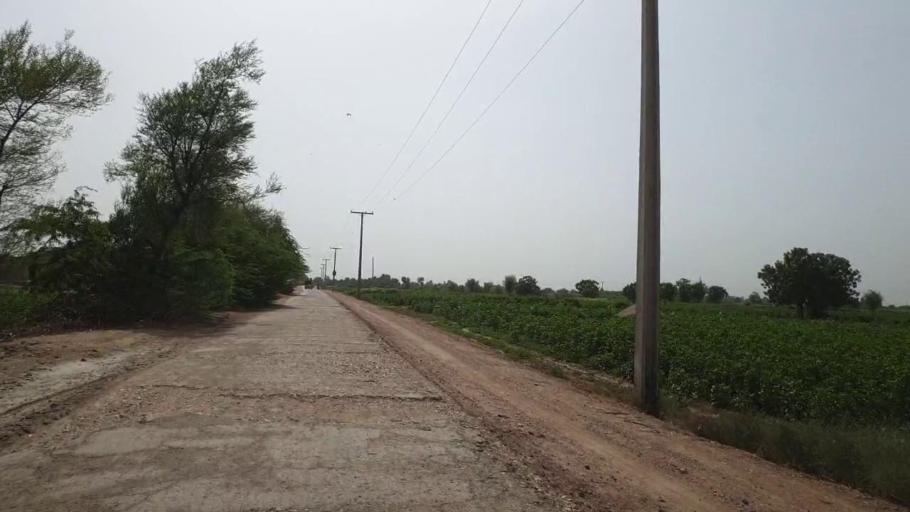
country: PK
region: Sindh
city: Bandhi
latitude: 26.5712
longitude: 68.3789
